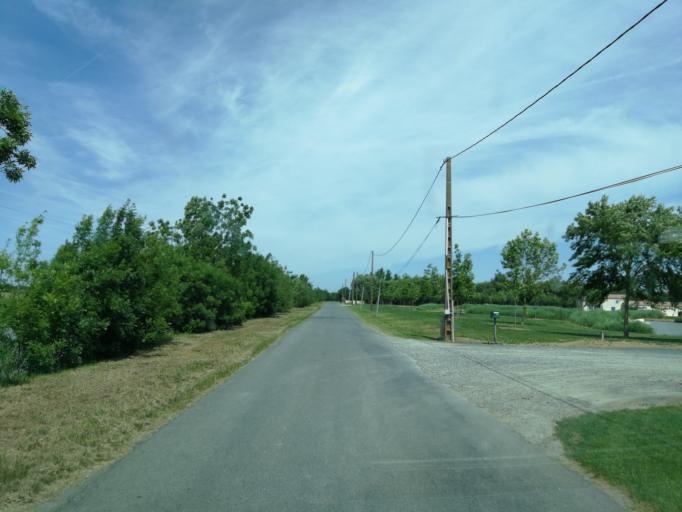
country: FR
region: Pays de la Loire
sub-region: Departement de la Vendee
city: Le Langon
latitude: 46.3915
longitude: -0.9369
